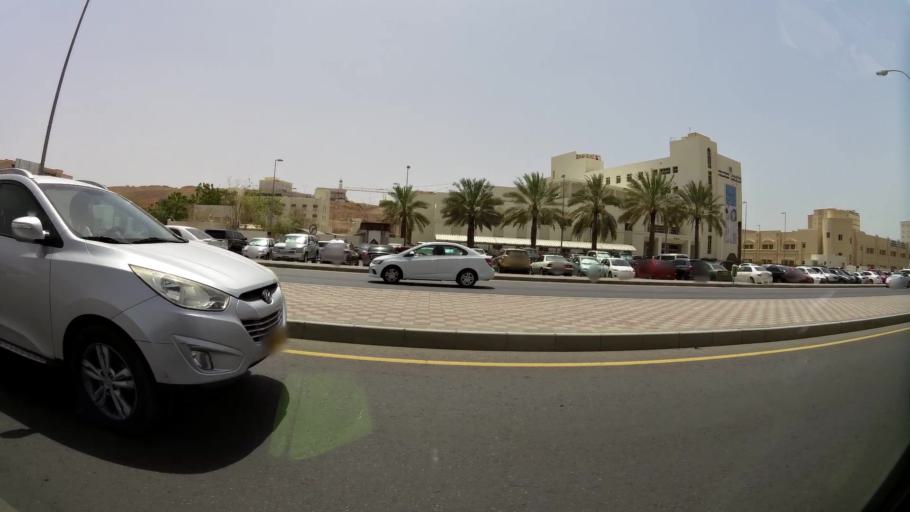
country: OM
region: Muhafazat Masqat
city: Bawshar
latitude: 23.5533
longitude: 58.4004
